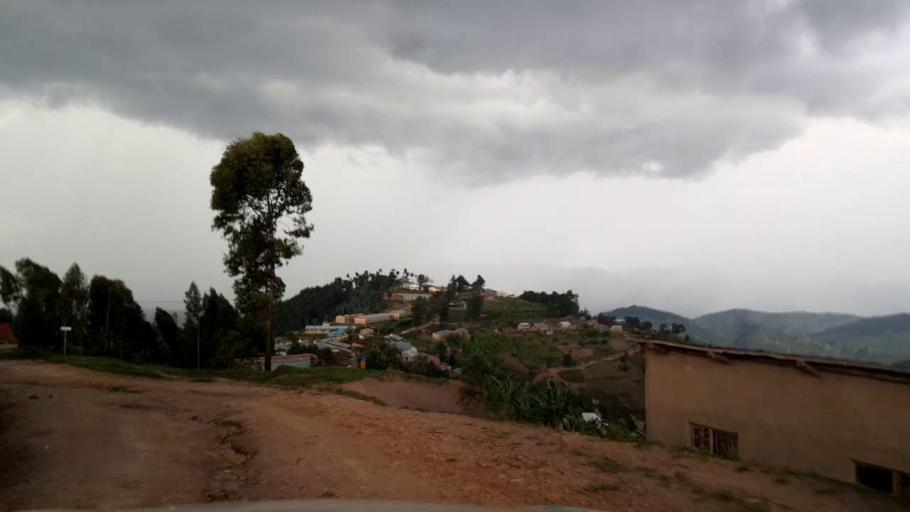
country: RW
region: Southern Province
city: Gitarama
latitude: -1.8721
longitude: 29.5886
